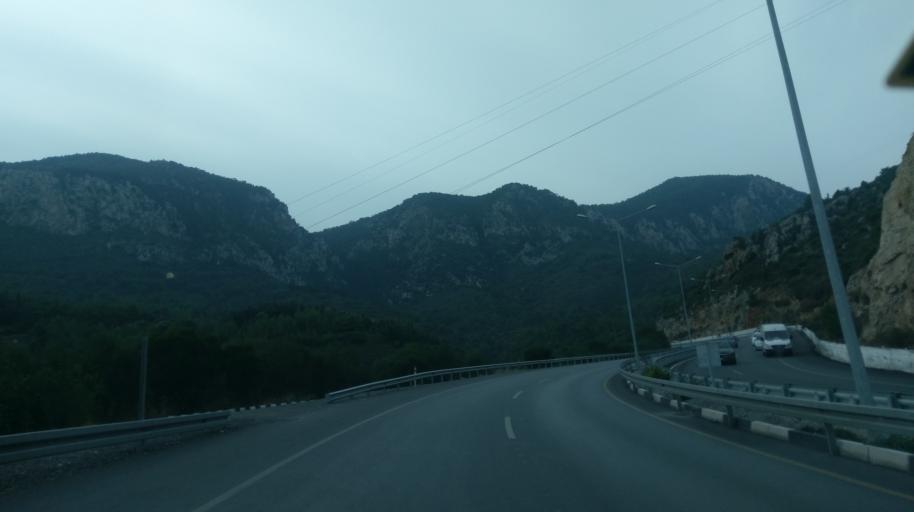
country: CY
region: Keryneia
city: Kyrenia
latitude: 35.3106
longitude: 33.3239
